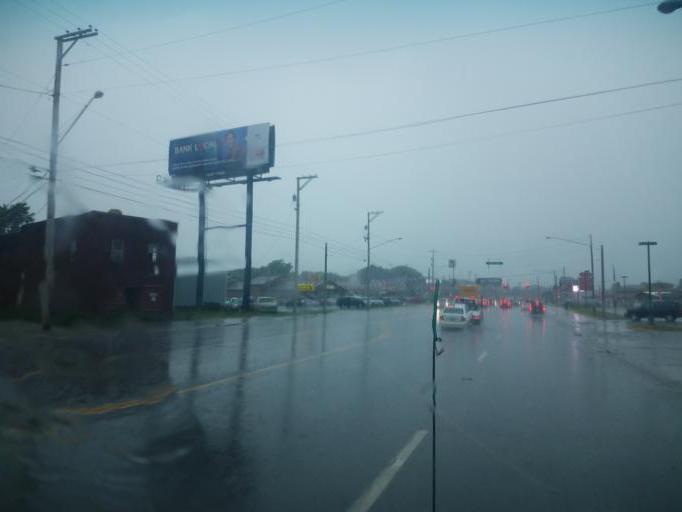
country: US
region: Ohio
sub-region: Stark County
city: Genoa
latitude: 40.7930
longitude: -81.4442
